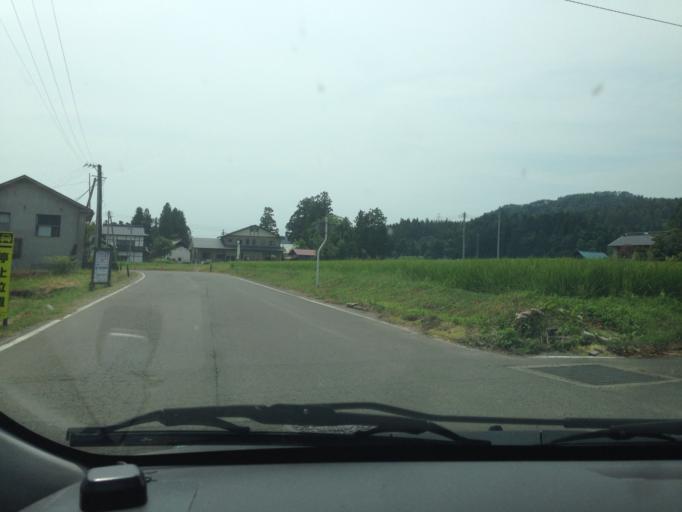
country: JP
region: Fukushima
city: Kitakata
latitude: 37.7030
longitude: 139.8458
